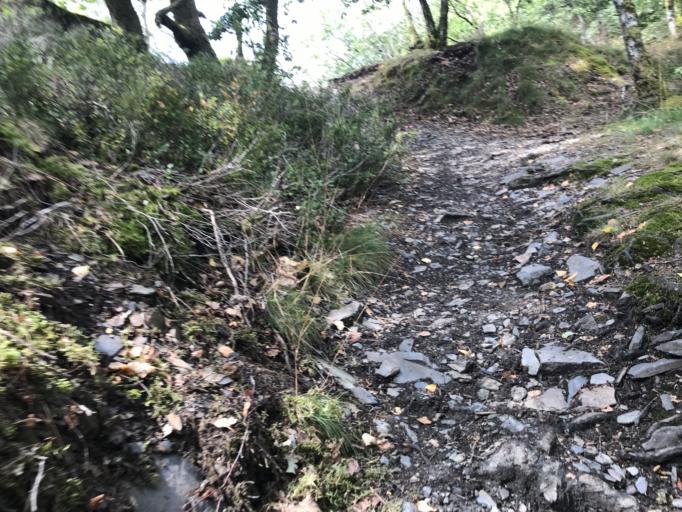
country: FR
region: Champagne-Ardenne
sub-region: Departement des Ardennes
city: Montherme
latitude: 49.8910
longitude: 4.7400
